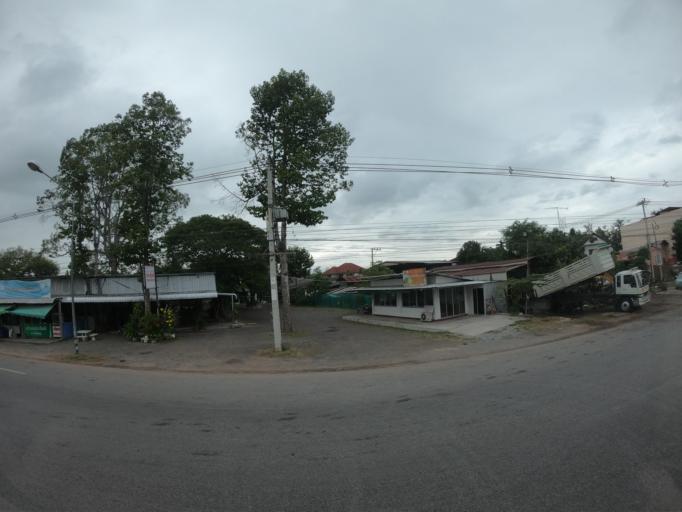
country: TH
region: Roi Et
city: Roi Et
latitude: 16.0444
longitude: 103.6345
